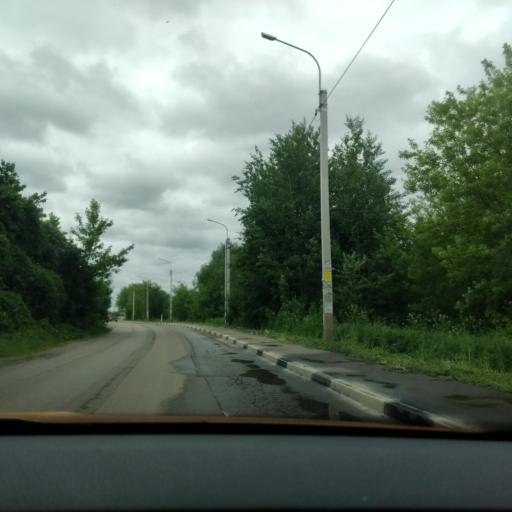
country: RU
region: Moskovskaya
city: Vereya
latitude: 55.6059
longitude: 38.0457
